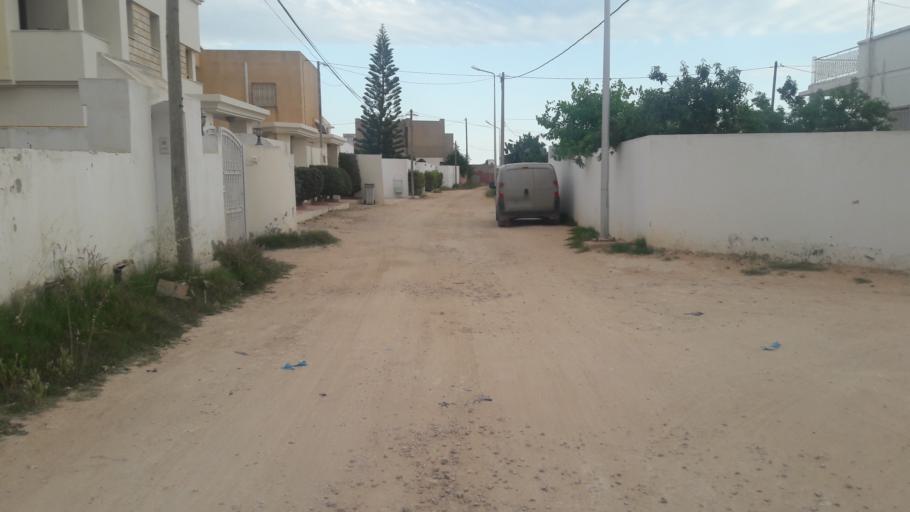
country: TN
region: Safaqis
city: Al Qarmadah
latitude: 34.8130
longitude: 10.7461
